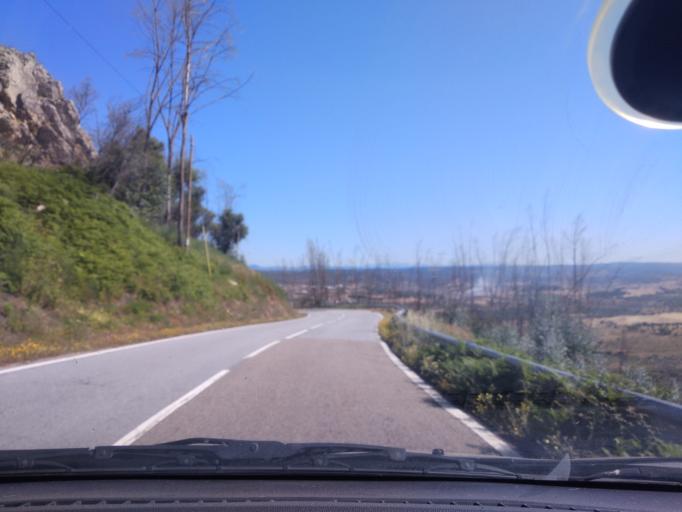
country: PT
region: Portalegre
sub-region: Nisa
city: Nisa
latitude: 39.6285
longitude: -7.6630
